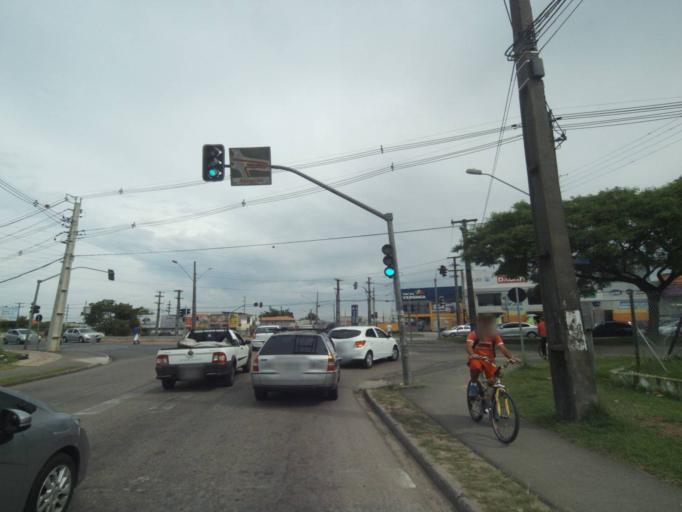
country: BR
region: Parana
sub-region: Pinhais
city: Pinhais
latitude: -25.4309
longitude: -49.2039
